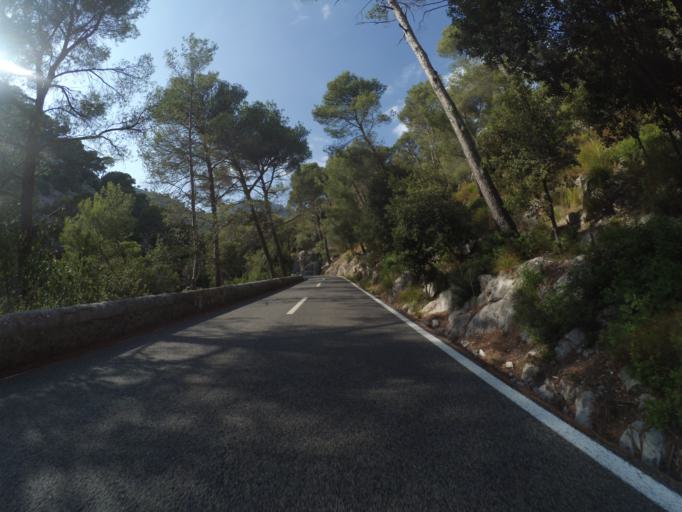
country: ES
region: Balearic Islands
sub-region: Illes Balears
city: Selva
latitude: 39.7855
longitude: 2.8953
